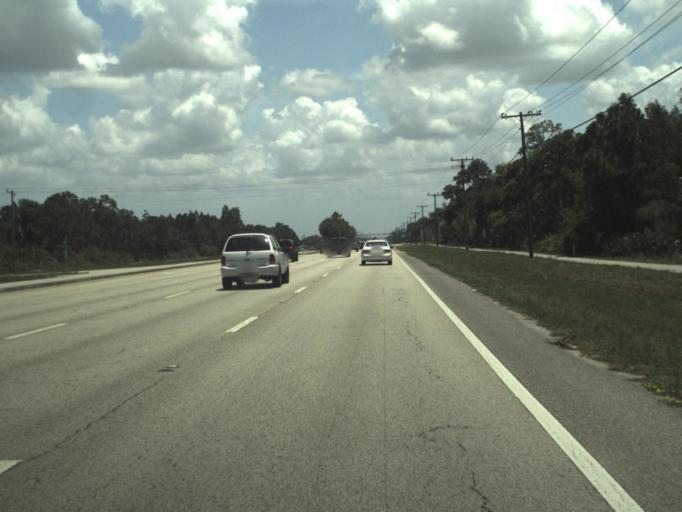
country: US
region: Florida
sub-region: Martin County
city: Port Salerno
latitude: 27.1594
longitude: -80.2232
